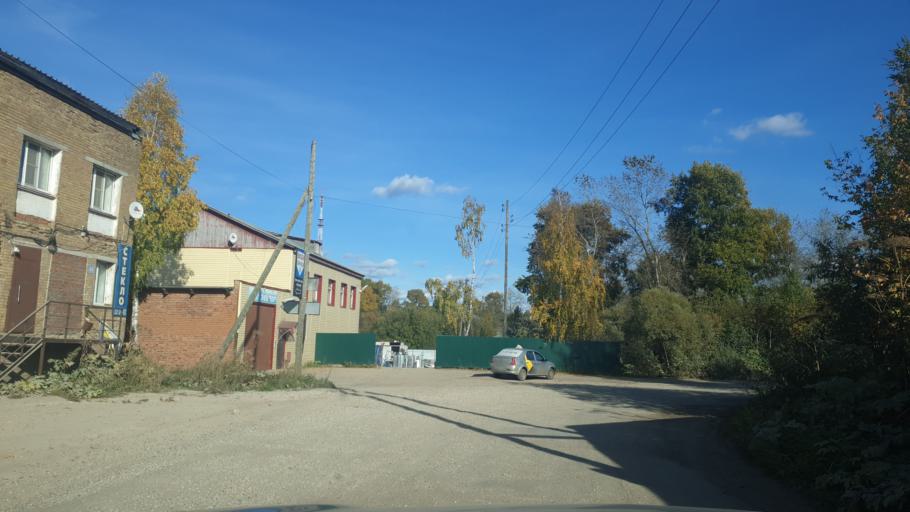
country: RU
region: Komi Republic
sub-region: Syktyvdinskiy Rayon
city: Syktyvkar
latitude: 61.6851
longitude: 50.7942
